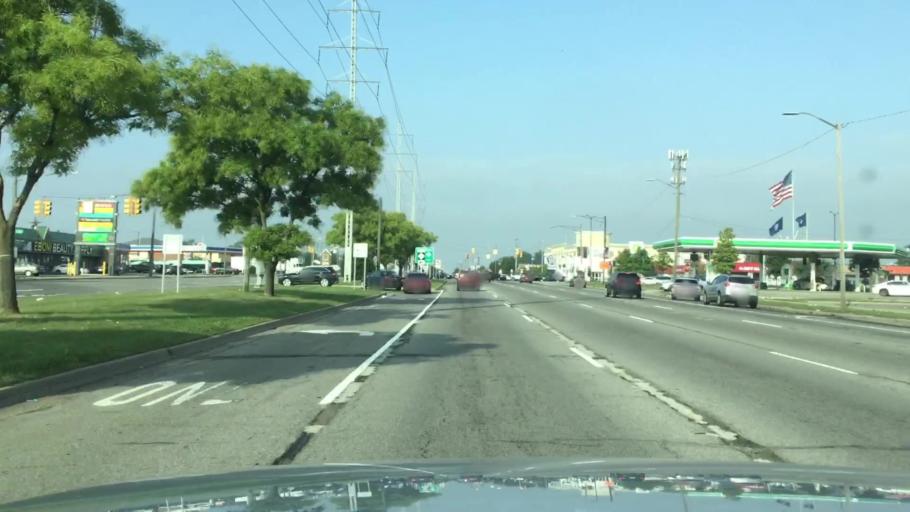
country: US
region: Michigan
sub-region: Macomb County
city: Eastpointe
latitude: 42.4501
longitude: -82.9654
